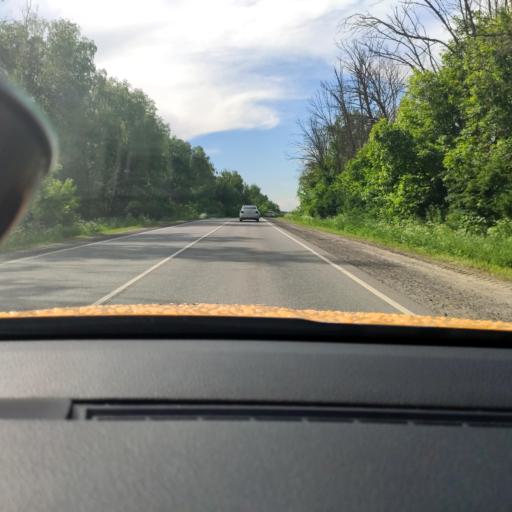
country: RU
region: Moskovskaya
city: Zhilevo
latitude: 54.9597
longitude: 37.9923
